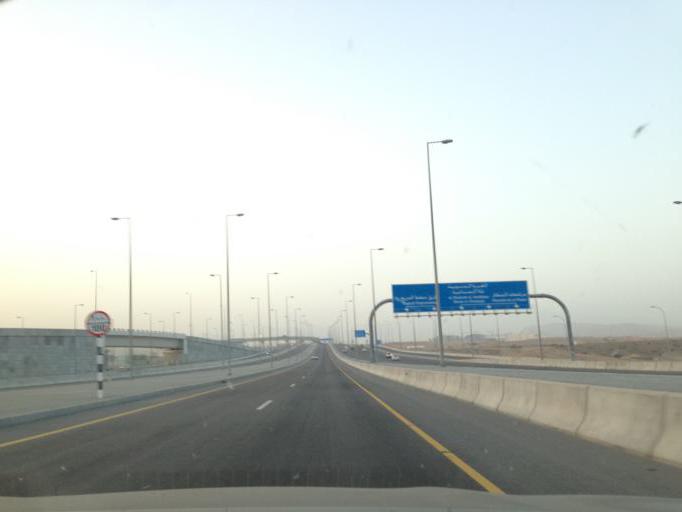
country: OM
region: Muhafazat Masqat
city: Bawshar
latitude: 23.5896
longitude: 58.3325
